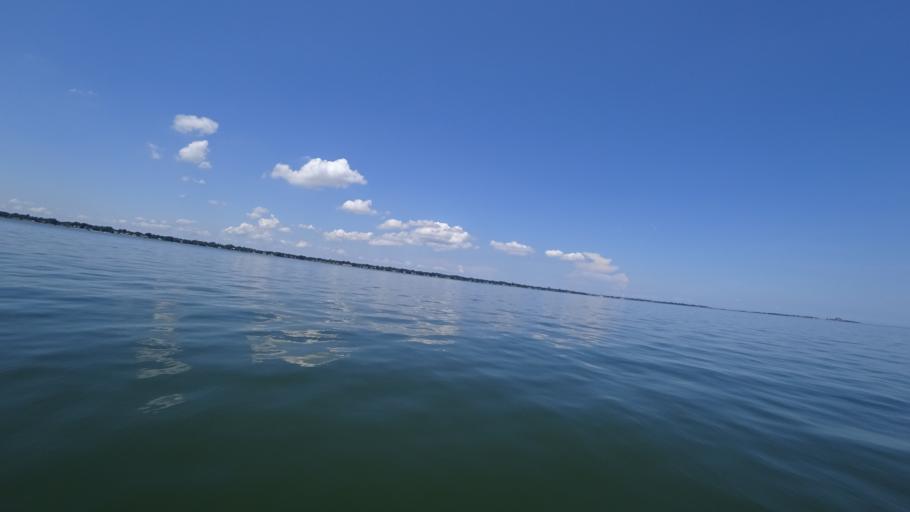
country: US
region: Virginia
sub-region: City of Hampton
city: Hampton
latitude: 36.9790
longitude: -76.3684
